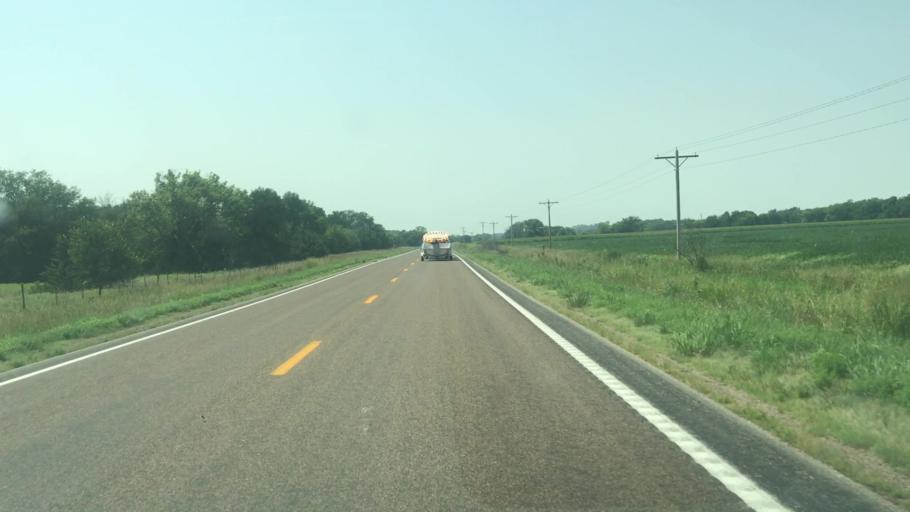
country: US
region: Nebraska
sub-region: Buffalo County
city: Ravenna
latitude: 41.0760
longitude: -98.6765
